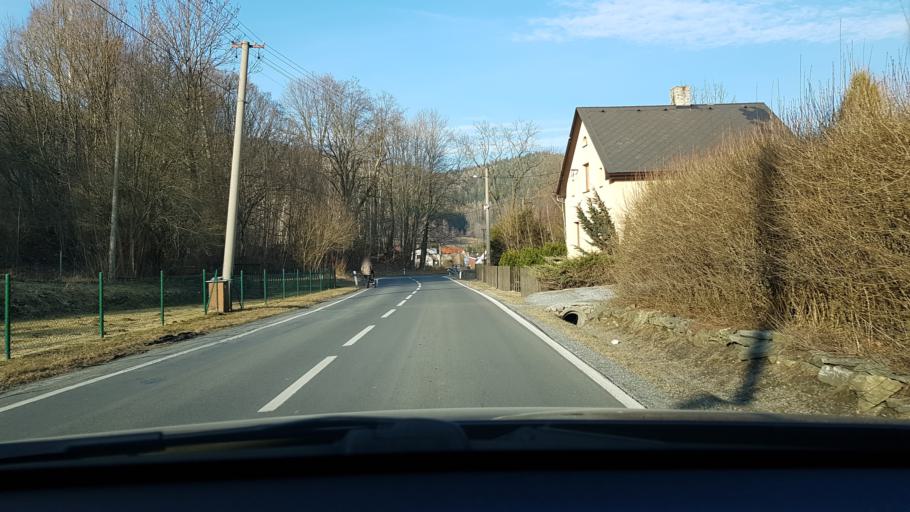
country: CZ
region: Olomoucky
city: Vapenna
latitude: 50.2195
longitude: 17.1061
